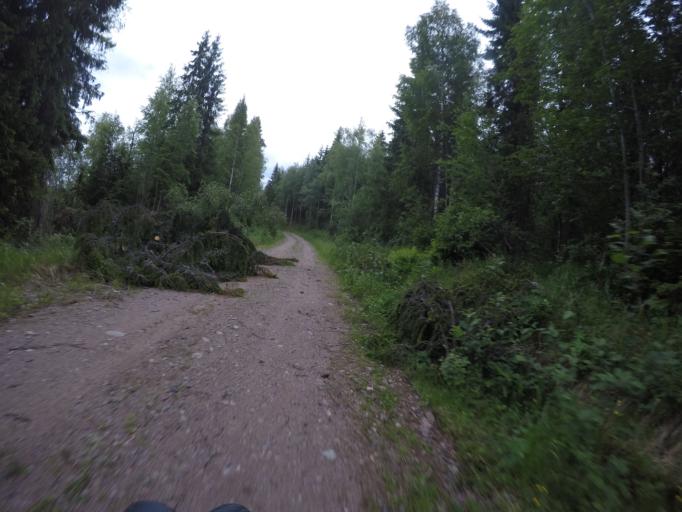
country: SE
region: Dalarna
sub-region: Ludvika Kommun
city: Abborrberget
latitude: 60.0374
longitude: 14.5957
